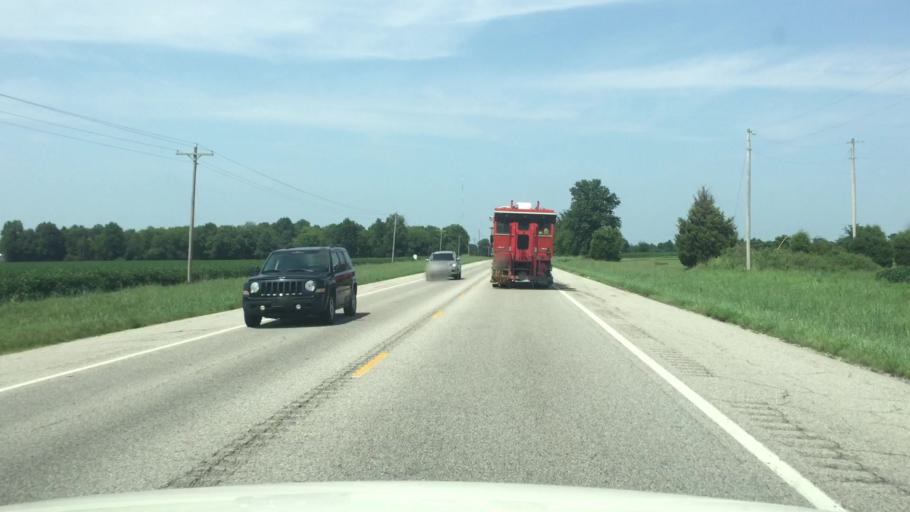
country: US
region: Kansas
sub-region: Cherokee County
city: Galena
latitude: 37.1880
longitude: -94.7045
